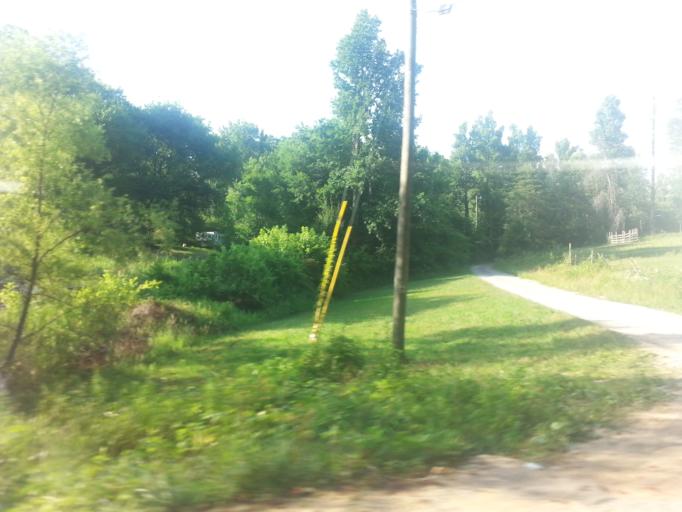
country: US
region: Tennessee
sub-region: Knox County
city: Knoxville
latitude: 35.9198
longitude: -83.9146
